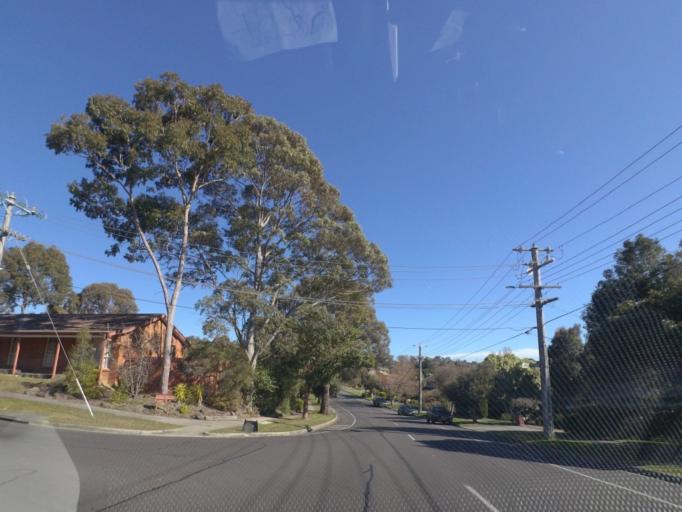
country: AU
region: Victoria
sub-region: Maroondah
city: Croydon Hills
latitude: -37.7804
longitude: 145.2646
